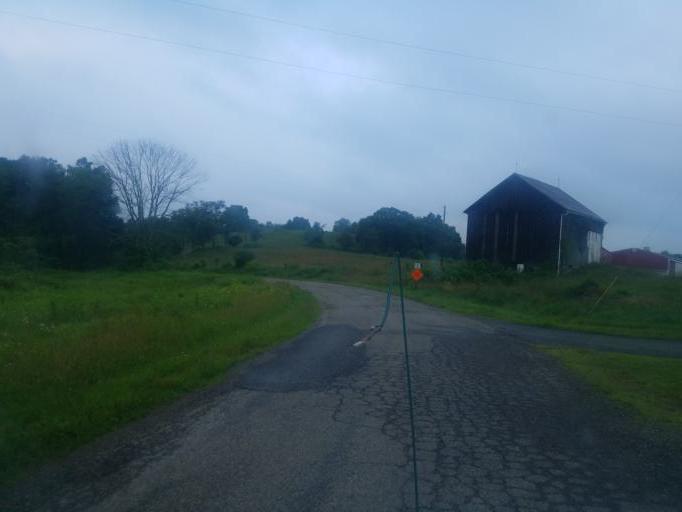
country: US
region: Ohio
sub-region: Columbiana County
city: Salineville
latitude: 40.6062
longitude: -80.9224
